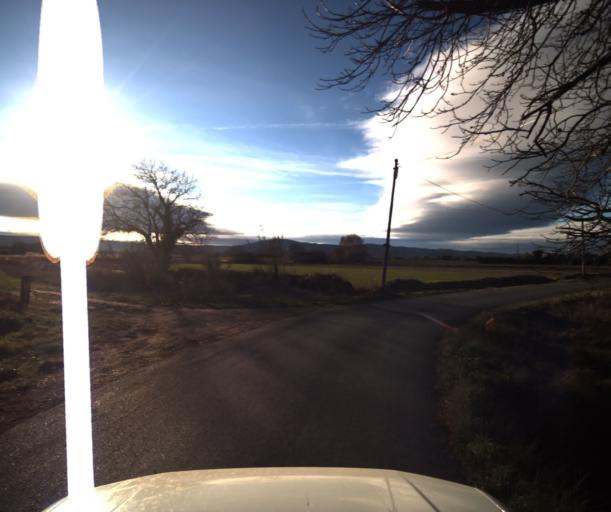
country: FR
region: Provence-Alpes-Cote d'Azur
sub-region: Departement du Vaucluse
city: Villelaure
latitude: 43.6918
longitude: 5.4604
